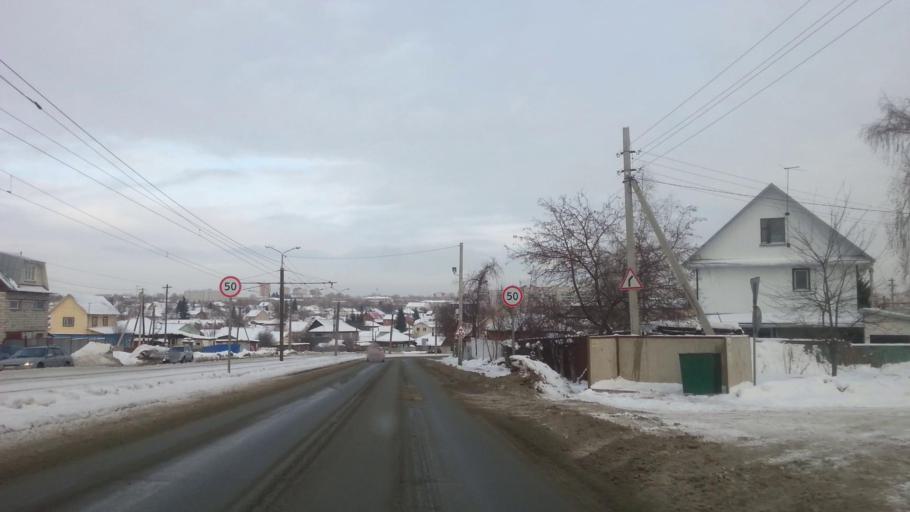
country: RU
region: Altai Krai
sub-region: Gorod Barnaulskiy
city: Barnaul
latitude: 53.3652
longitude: 83.7307
